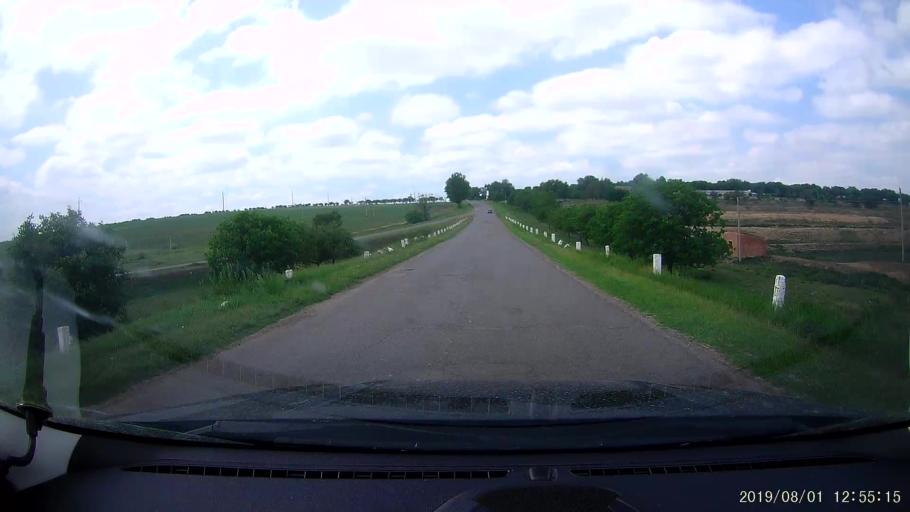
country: MD
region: Gagauzia
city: Vulcanesti
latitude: 45.6940
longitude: 28.4706
